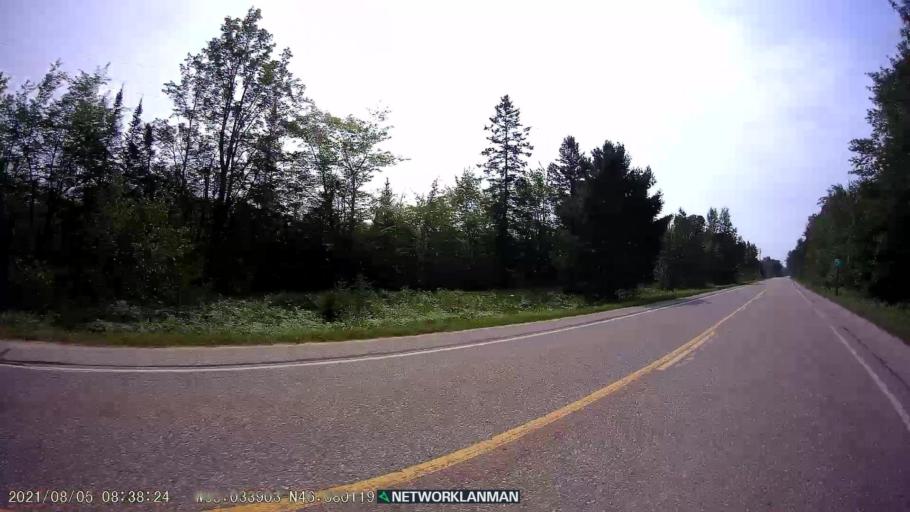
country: US
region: Michigan
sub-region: Luce County
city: Newberry
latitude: 46.6798
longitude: -85.0339
